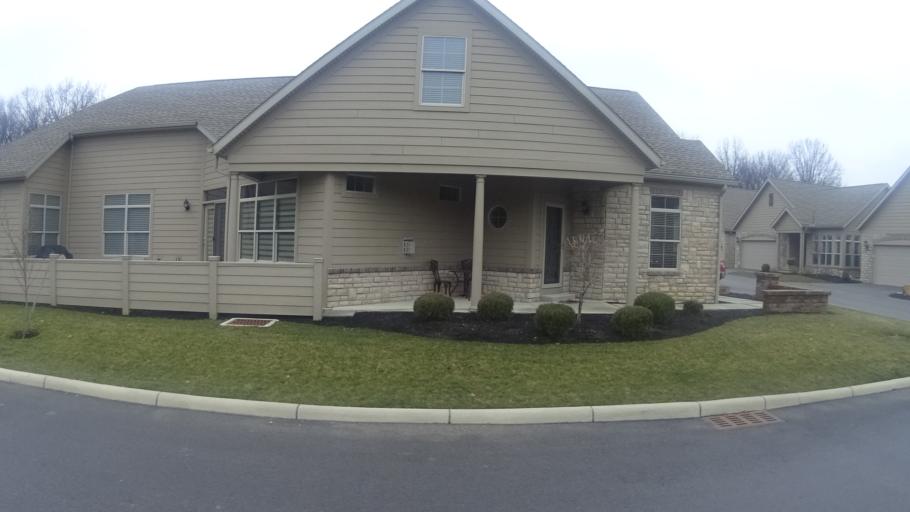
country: US
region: Ohio
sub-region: Erie County
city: Sandusky
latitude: 41.4073
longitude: -82.6377
